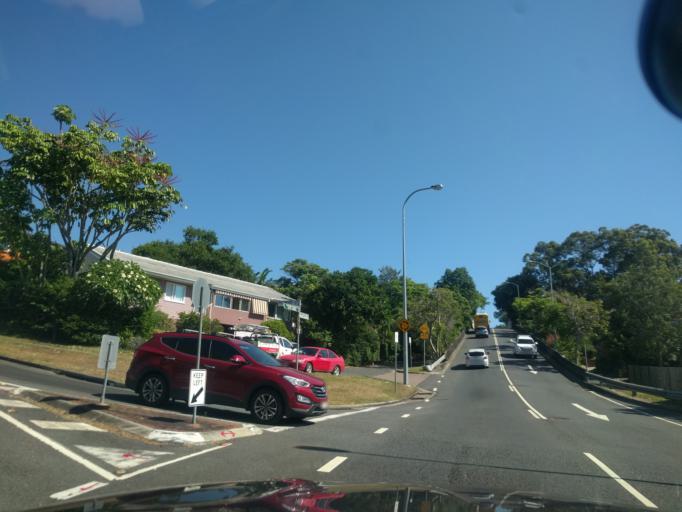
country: AU
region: Queensland
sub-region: Brisbane
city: Stafford
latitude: -27.4028
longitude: 153.0092
